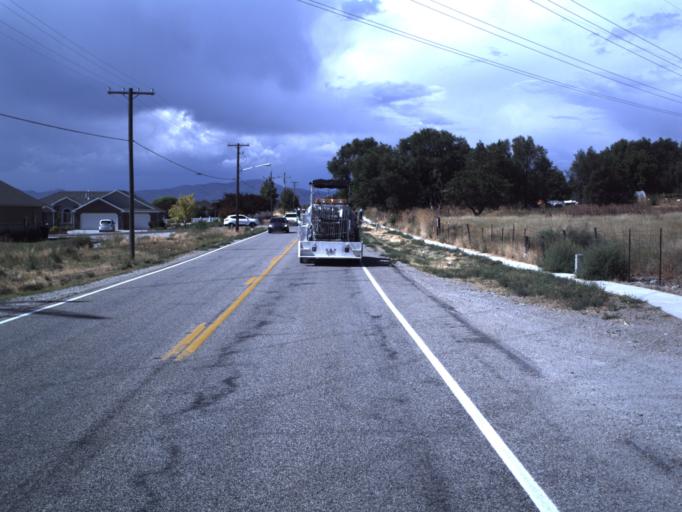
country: US
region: Utah
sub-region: Box Elder County
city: Honeyville
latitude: 41.6225
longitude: -112.0719
